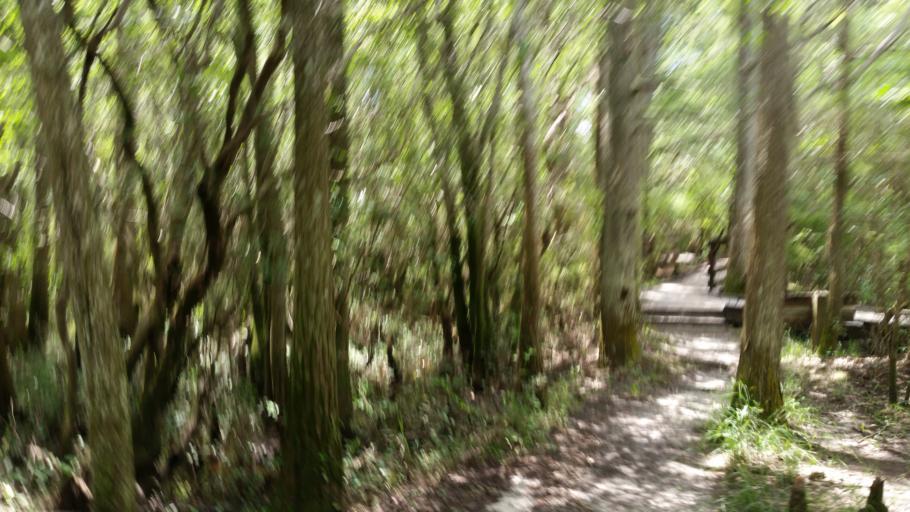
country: US
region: Florida
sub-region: Santa Rosa County
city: East Milton
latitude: 30.7052
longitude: -86.8812
